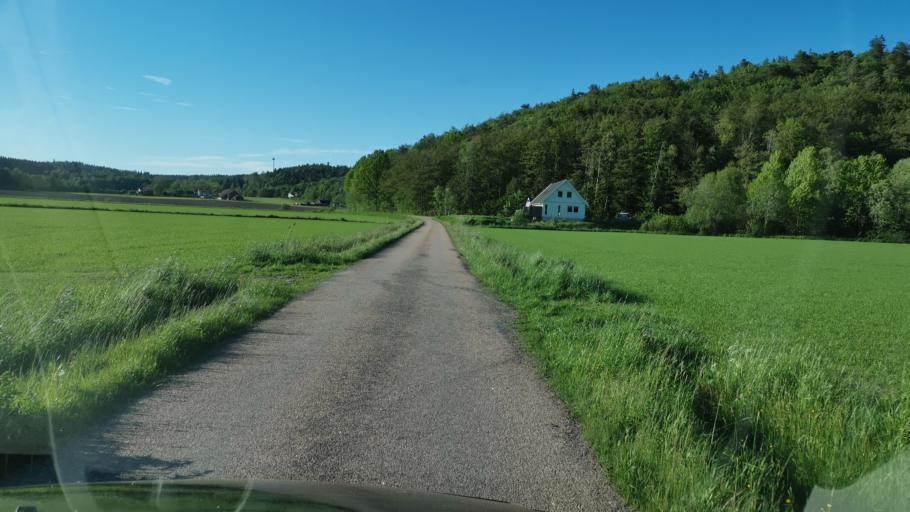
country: SE
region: Vaestra Goetaland
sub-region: Orust
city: Henan
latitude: 58.2831
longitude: 11.6407
